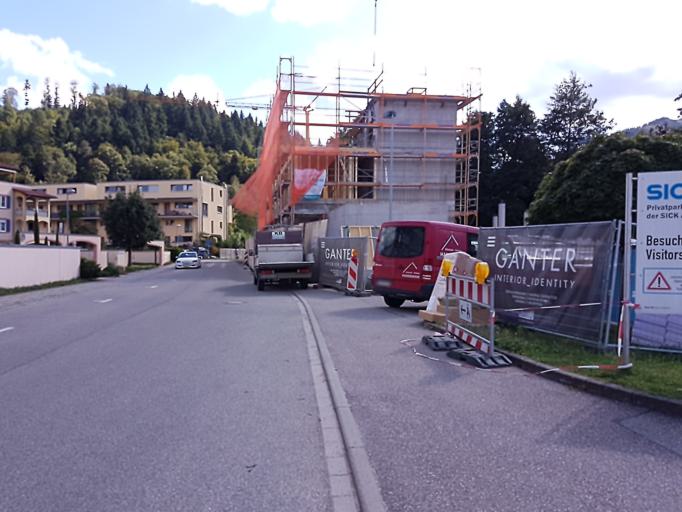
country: DE
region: Baden-Wuerttemberg
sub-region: Freiburg Region
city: Waldkirch
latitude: 48.0881
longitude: 7.9507
